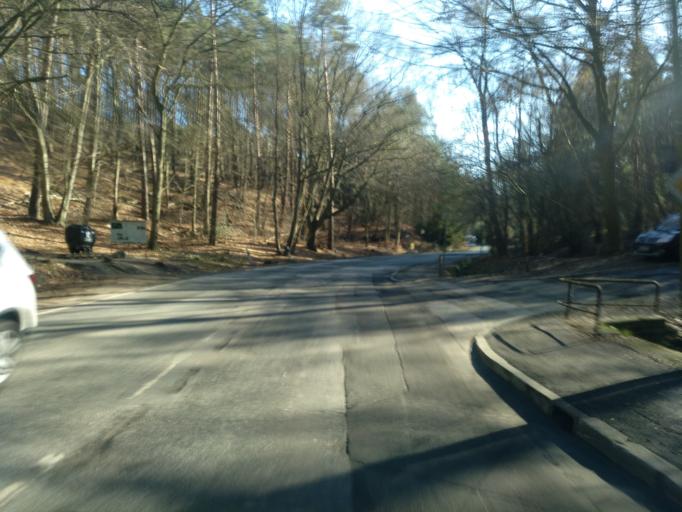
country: DE
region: Hamburg
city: Harburg
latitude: 53.4570
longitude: 9.8944
